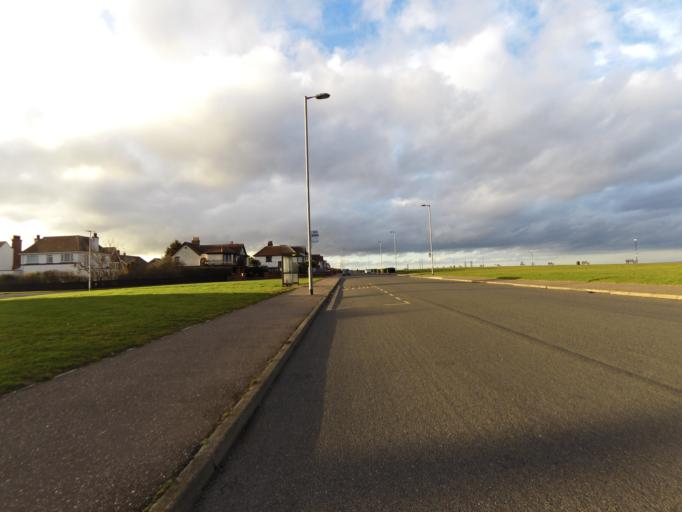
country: GB
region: England
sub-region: Norfolk
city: Gorleston-on-Sea
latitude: 52.5602
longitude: 1.7310
